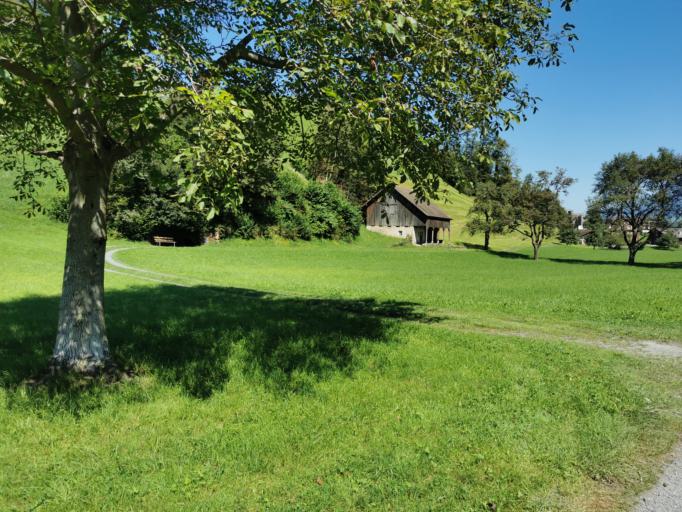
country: CH
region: Uri
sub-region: Uri
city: Attinghausen
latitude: 46.8566
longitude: 8.6332
